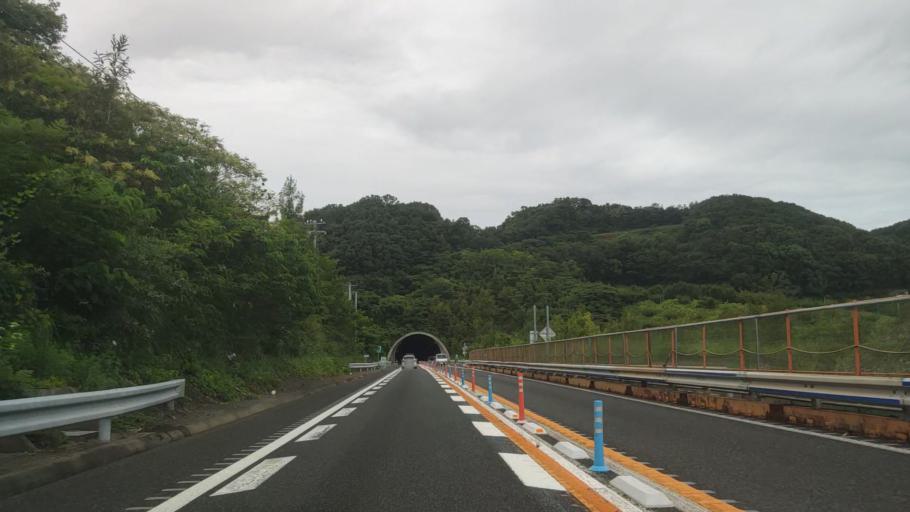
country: JP
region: Wakayama
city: Tanabe
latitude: 33.7846
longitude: 135.3129
